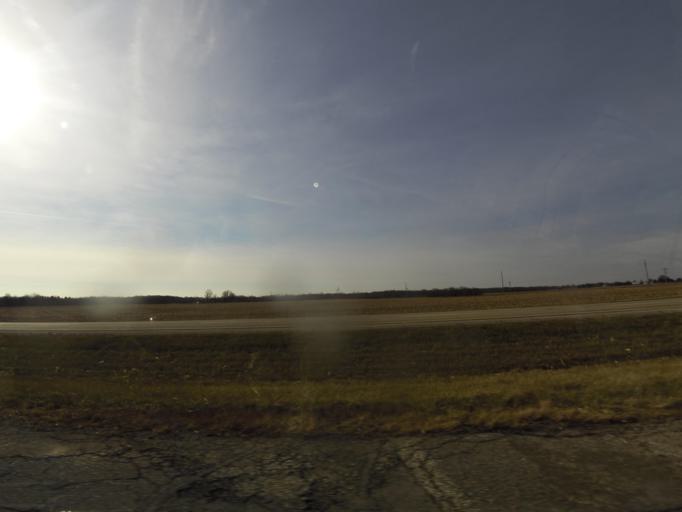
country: US
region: Illinois
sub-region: De Witt County
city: Clinton
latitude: 40.1382
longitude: -88.9768
